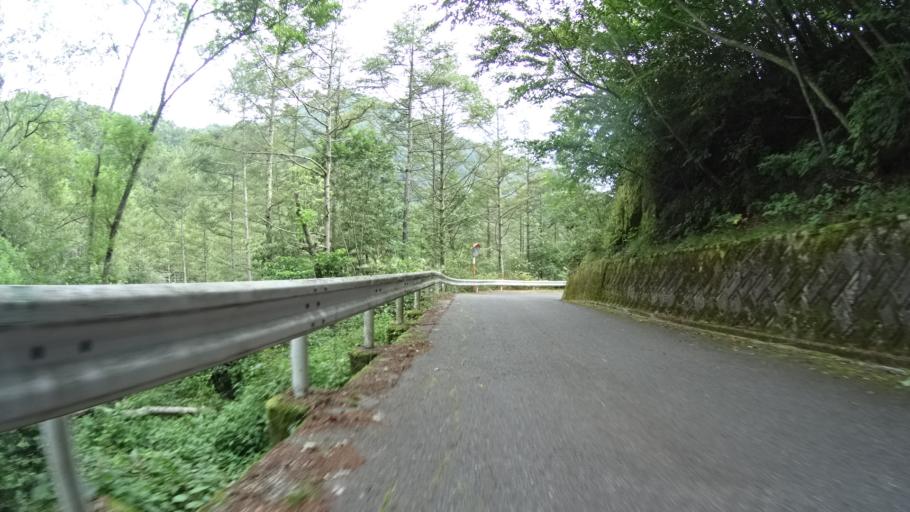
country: JP
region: Yamanashi
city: Nirasaki
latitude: 35.8050
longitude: 138.5265
